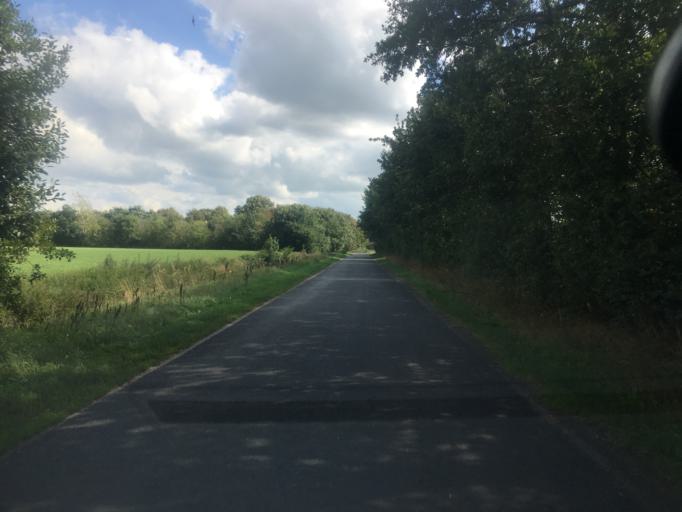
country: DK
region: South Denmark
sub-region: Tonder Kommune
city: Logumkloster
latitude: 55.0021
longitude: 9.0141
